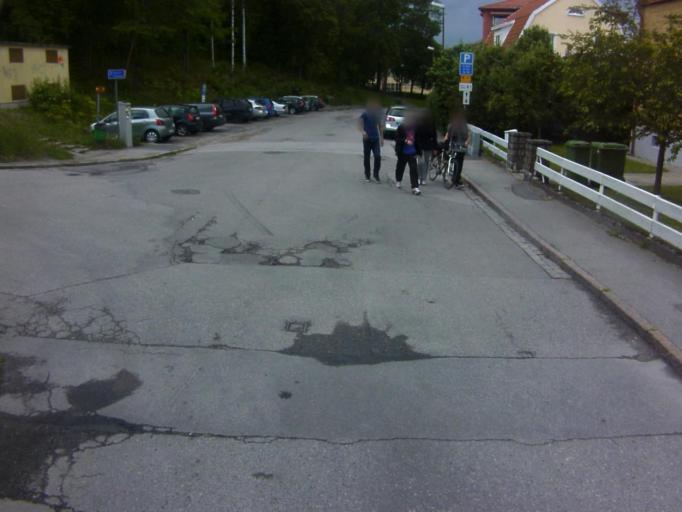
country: SE
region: Soedermanland
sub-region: Eskilstuna Kommun
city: Eskilstuna
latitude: 59.3617
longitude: 16.5156
